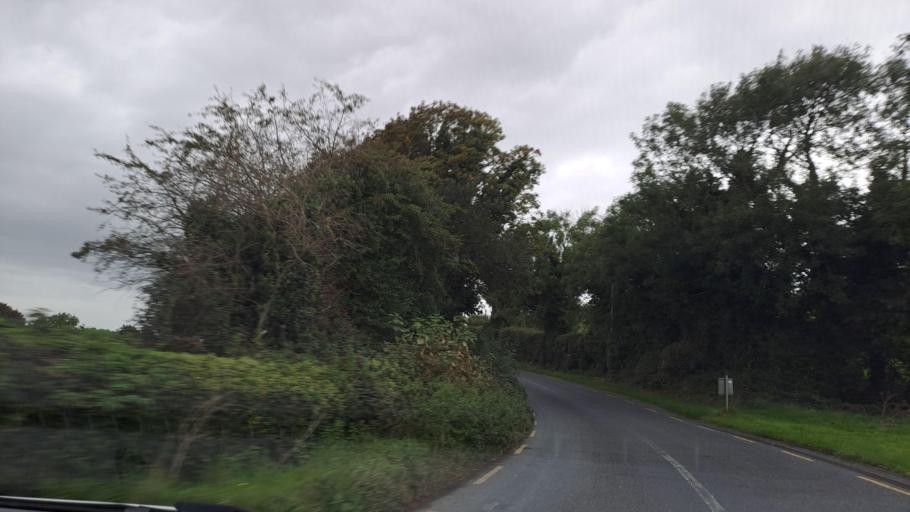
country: IE
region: Ulster
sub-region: An Cabhan
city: Bailieborough
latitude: 54.0038
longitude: -6.9064
